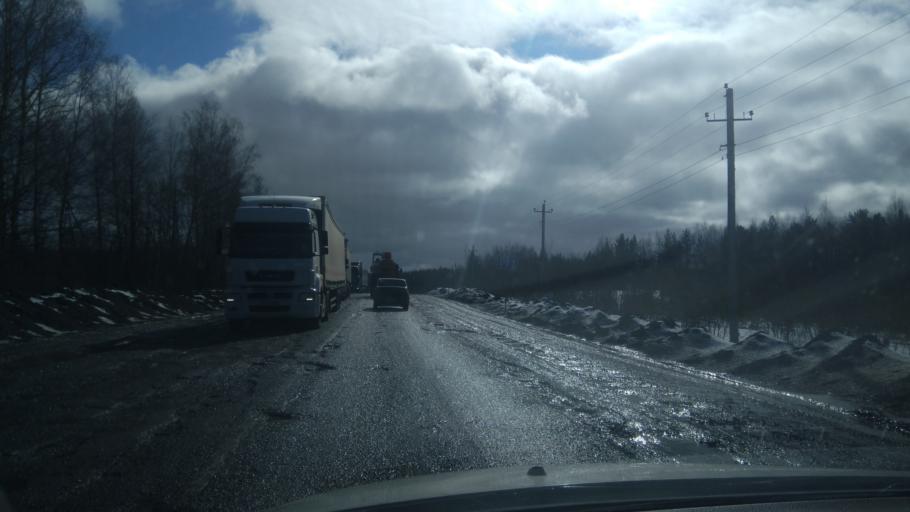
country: RU
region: Perm
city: Suksun
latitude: 57.0879
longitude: 57.3962
